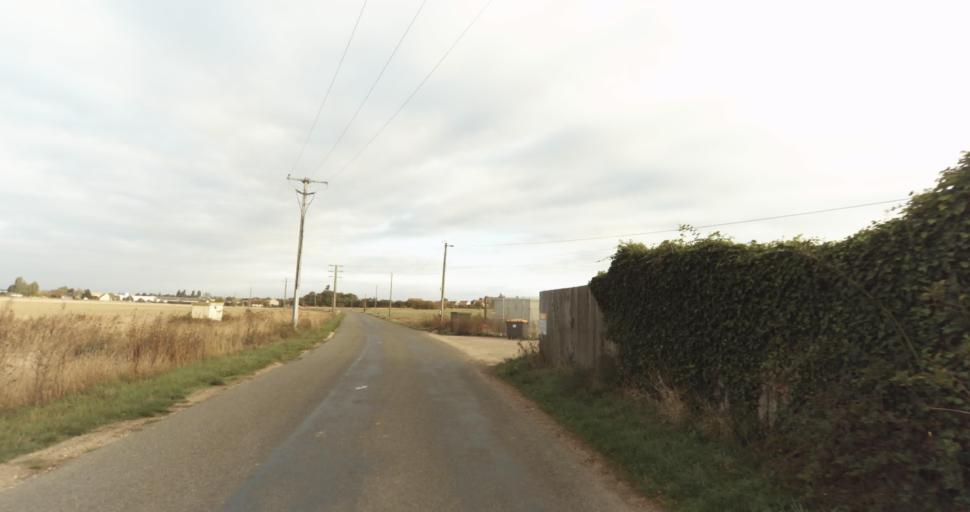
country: FR
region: Centre
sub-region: Departement d'Eure-et-Loir
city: Vernouillet
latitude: 48.7098
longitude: 1.3824
